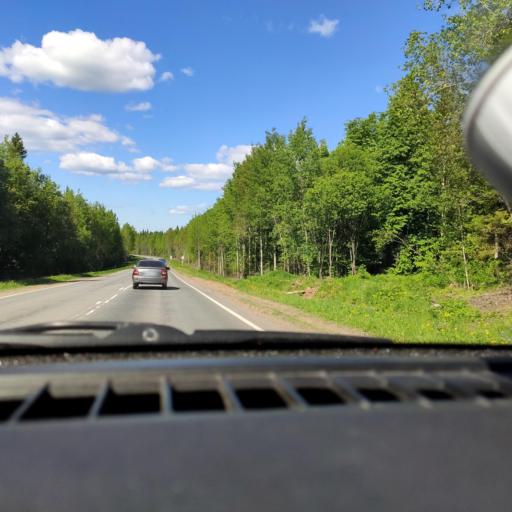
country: RU
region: Perm
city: Polazna
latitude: 58.2597
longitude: 56.1660
